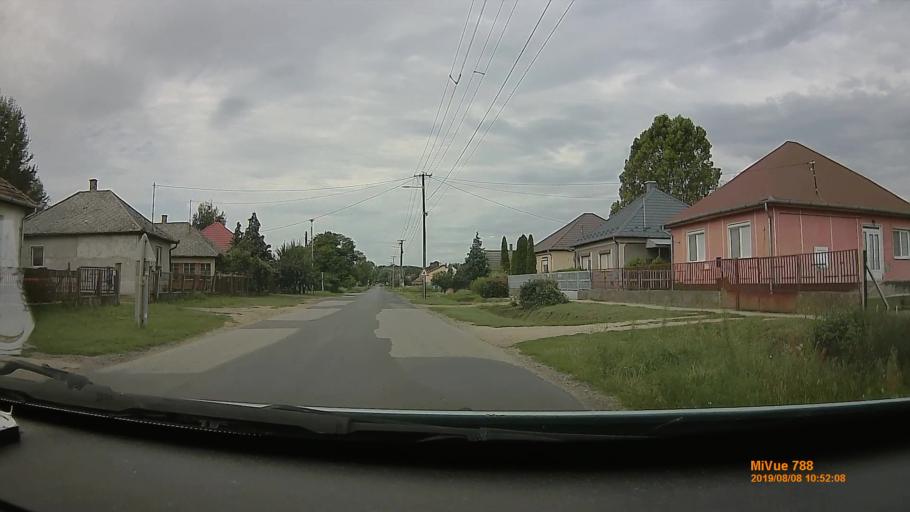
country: HU
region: Szabolcs-Szatmar-Bereg
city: Balkany
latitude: 47.7702
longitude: 21.8464
